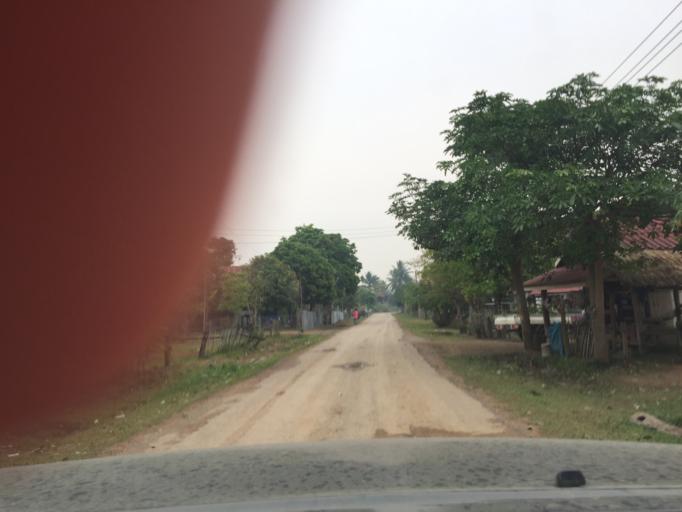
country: LA
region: Xiagnabouli
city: Sainyabuli
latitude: 19.0815
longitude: 101.5251
